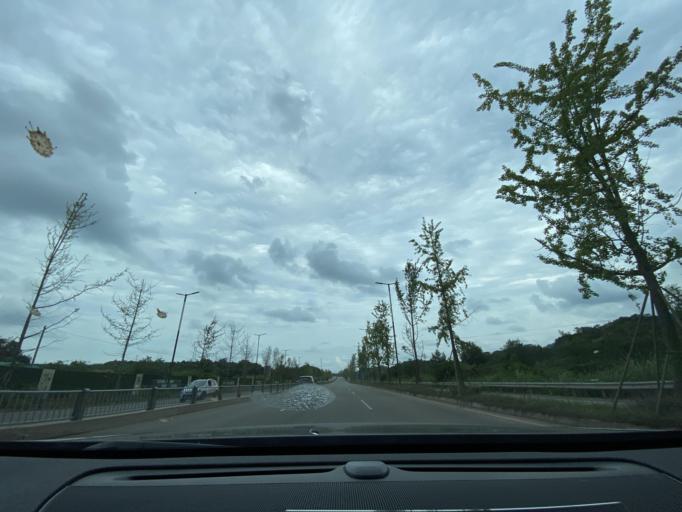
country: CN
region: Sichuan
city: Jiancheng
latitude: 30.4912
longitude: 104.4695
